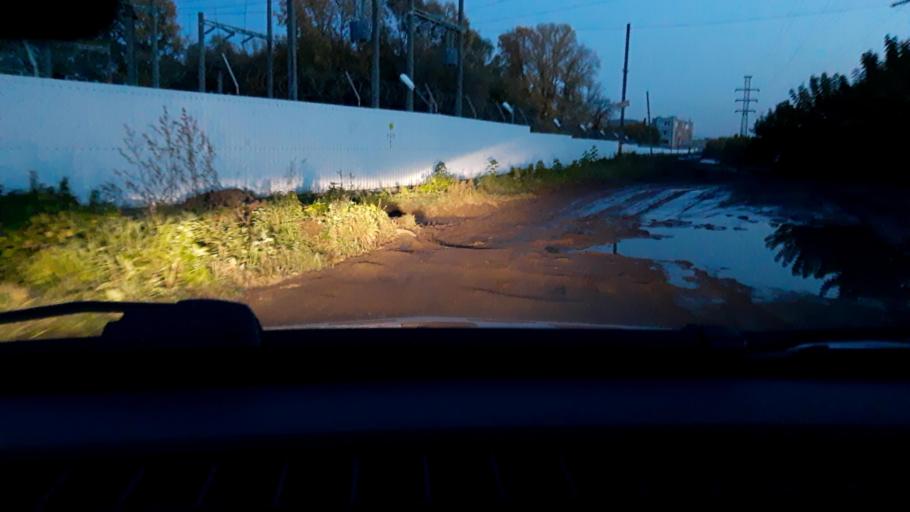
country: RU
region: Bashkortostan
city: Ufa
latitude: 54.8046
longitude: 56.0558
